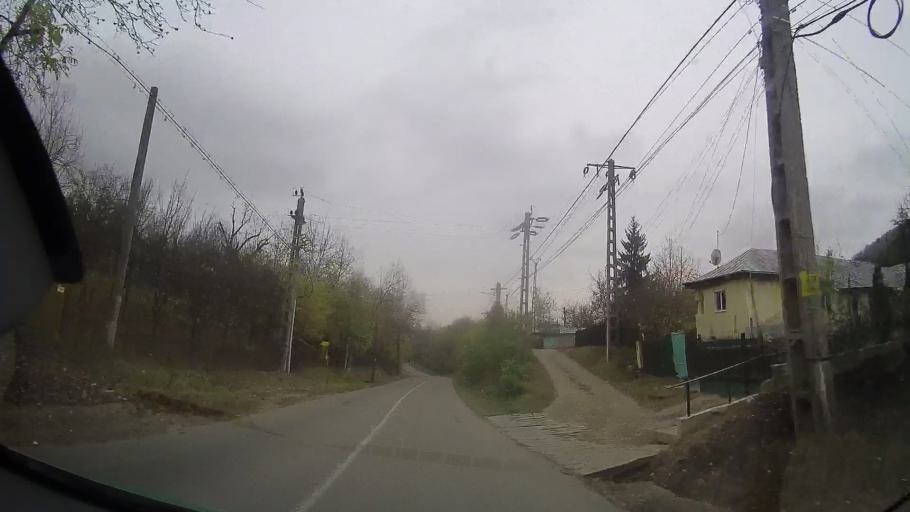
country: RO
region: Prahova
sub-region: Comuna Ceptura
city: Ceptura de Jos
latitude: 45.0336
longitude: 26.3193
